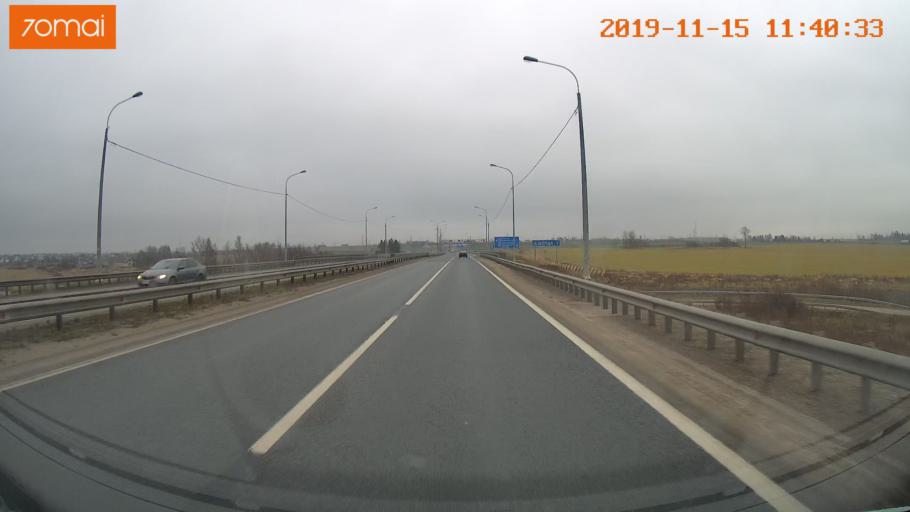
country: RU
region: Vologda
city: Molochnoye
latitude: 59.2126
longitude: 39.7543
